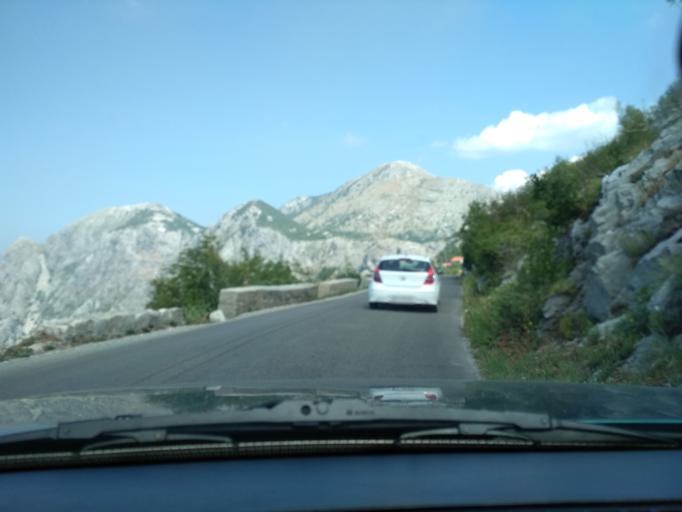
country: ME
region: Kotor
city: Kotor
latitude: 42.4151
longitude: 18.7917
